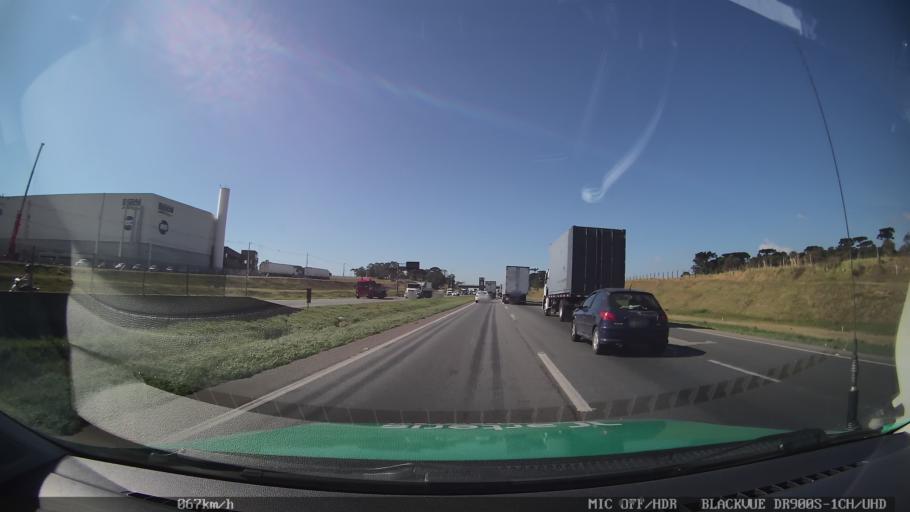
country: BR
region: Parana
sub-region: Sao Jose Dos Pinhais
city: Sao Jose dos Pinhais
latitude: -25.5458
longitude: -49.2976
